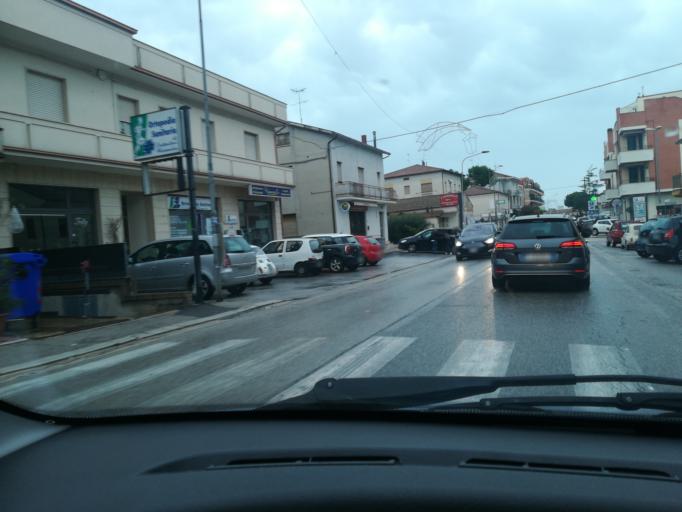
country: IT
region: The Marches
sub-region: Provincia di Macerata
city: Borgo Stazione
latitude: 43.2862
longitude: 13.6460
